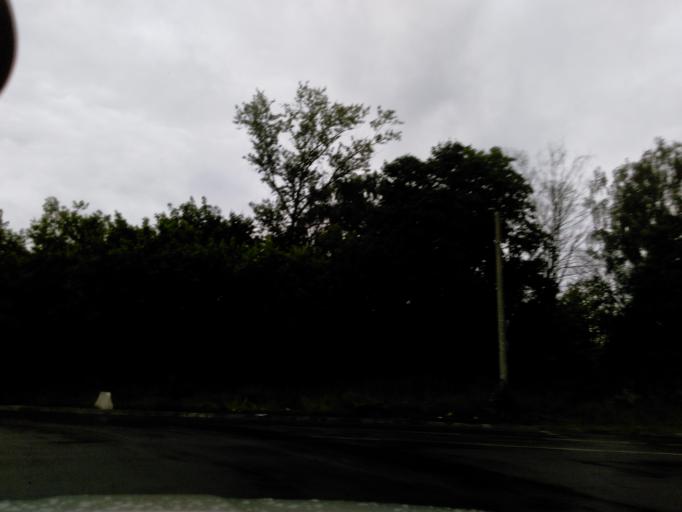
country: RU
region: Moscow
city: Zelenograd
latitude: 55.9703
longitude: 37.1840
